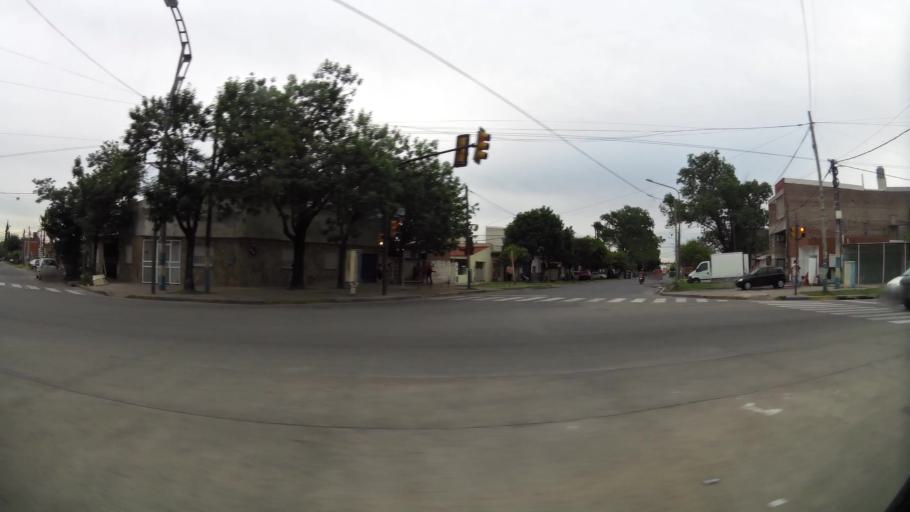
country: AR
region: Santa Fe
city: Granadero Baigorria
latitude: -32.9013
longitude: -60.7053
